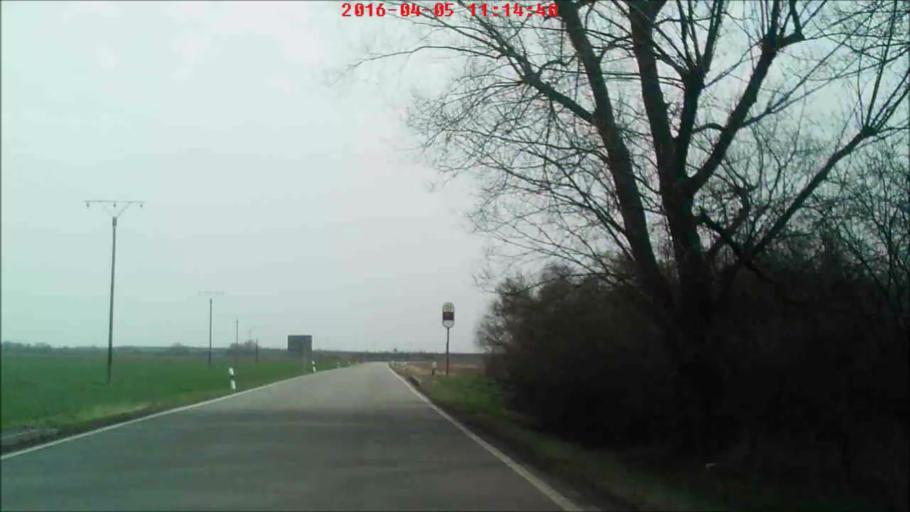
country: DE
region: Thuringia
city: Zimmernsupra
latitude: 50.9925
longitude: 10.8903
